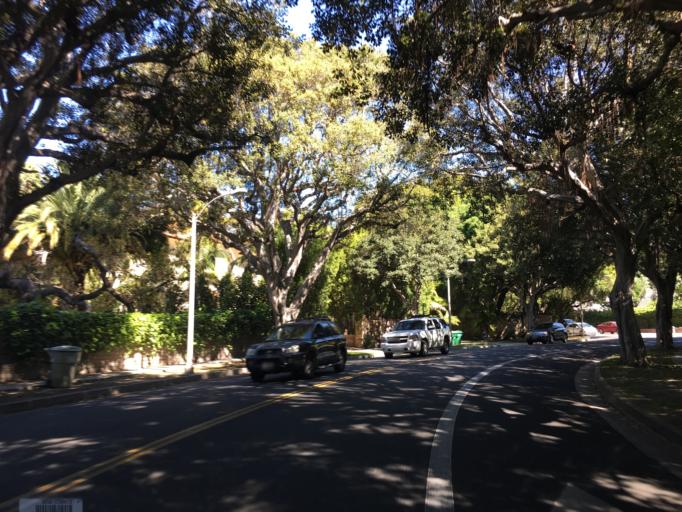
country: US
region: California
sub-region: Los Angeles County
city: Beverly Hills
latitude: 34.0866
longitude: -118.4131
